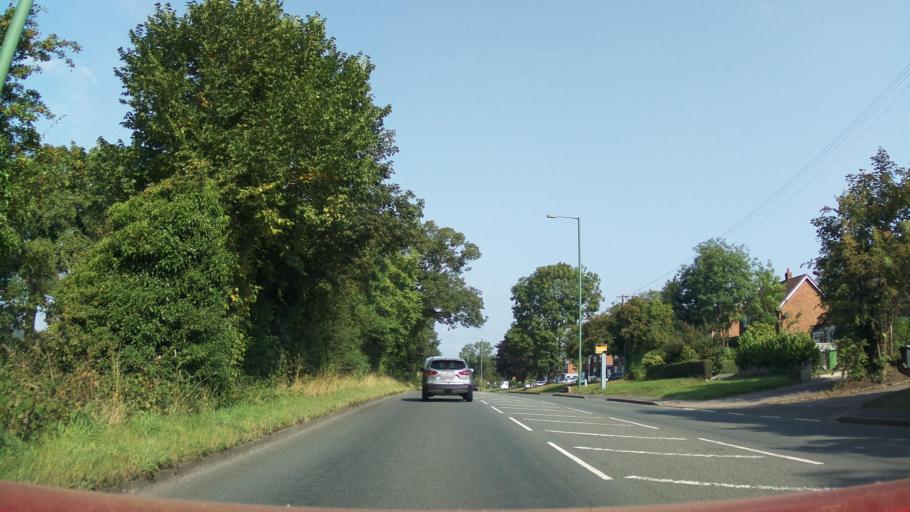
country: GB
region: England
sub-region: Walsall
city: Streetly
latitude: 52.5888
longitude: -1.8886
